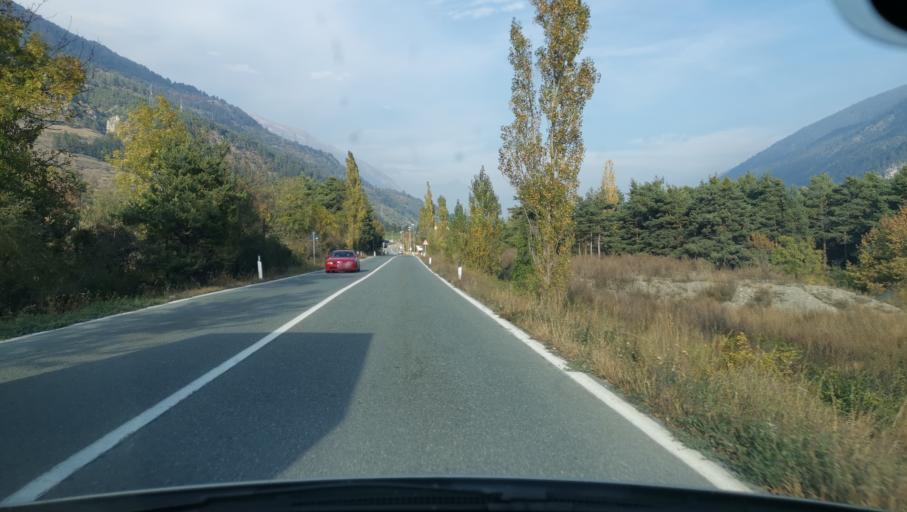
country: IT
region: Piedmont
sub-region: Provincia di Torino
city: Salbertrand
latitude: 45.0657
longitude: 6.8747
